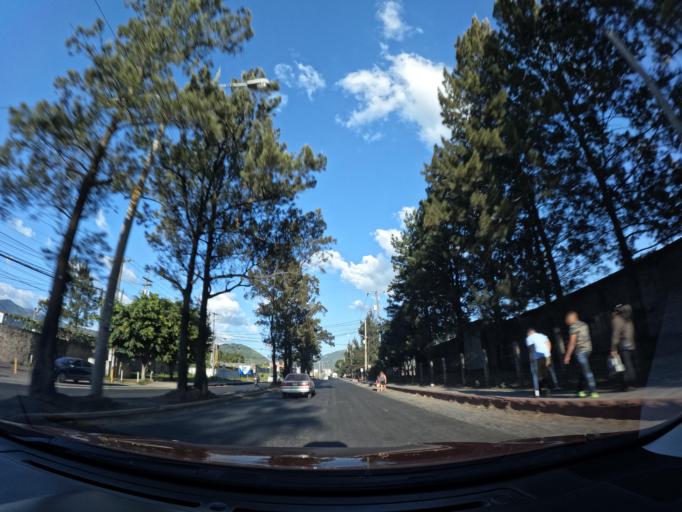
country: GT
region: Escuintla
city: Palin
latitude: 14.4080
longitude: -90.6869
